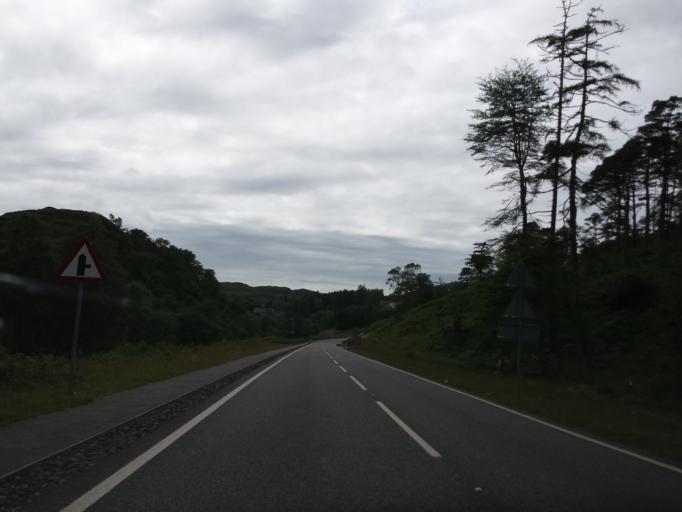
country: GB
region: Scotland
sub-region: Argyll and Bute
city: Isle Of Mull
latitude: 56.8991
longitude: -5.7783
